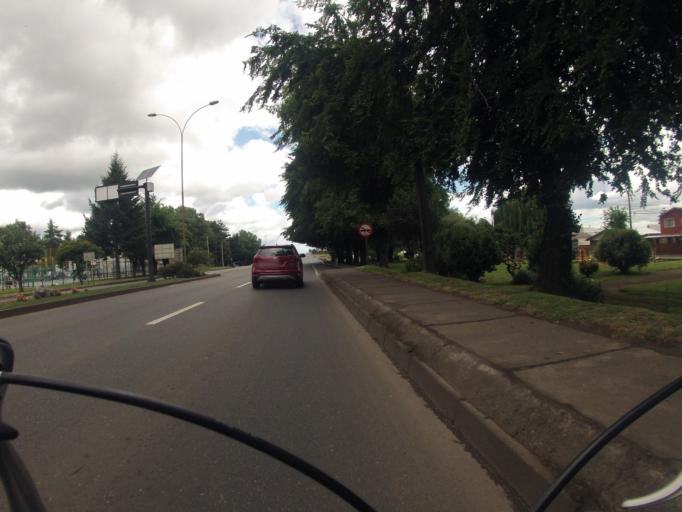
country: CL
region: Araucania
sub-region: Provincia de Cautin
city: Temuco
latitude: -38.7510
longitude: -72.6092
